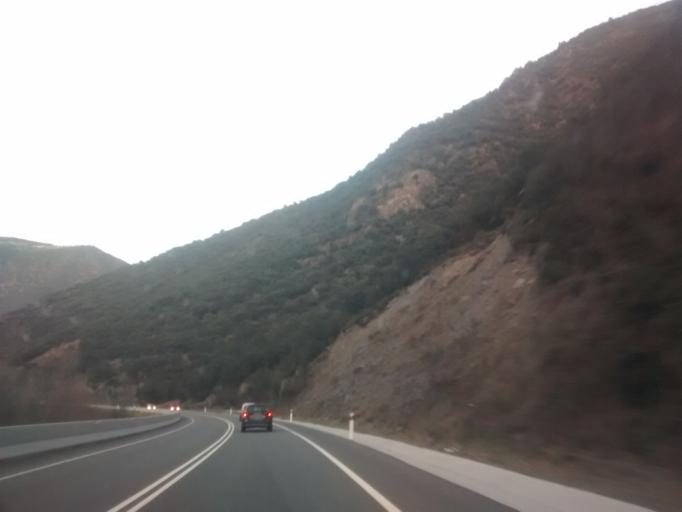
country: AD
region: Sant Julia de Loria
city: Sant Julia de Loria
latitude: 42.4158
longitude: 1.4648
